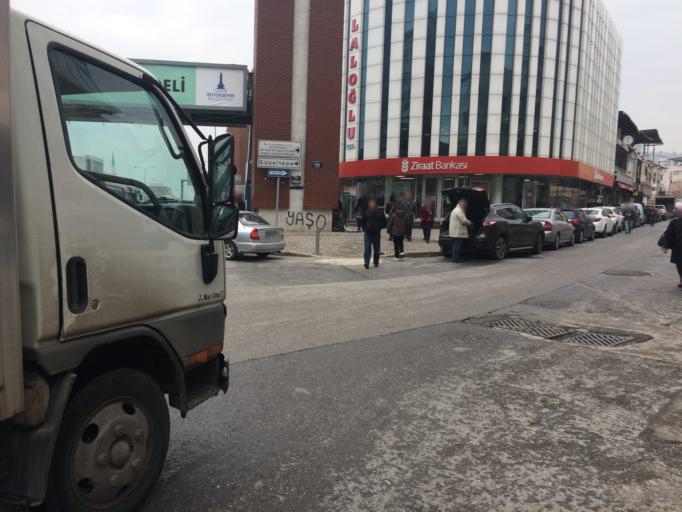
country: TR
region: Izmir
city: Karsiyaka
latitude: 38.4919
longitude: 27.0656
